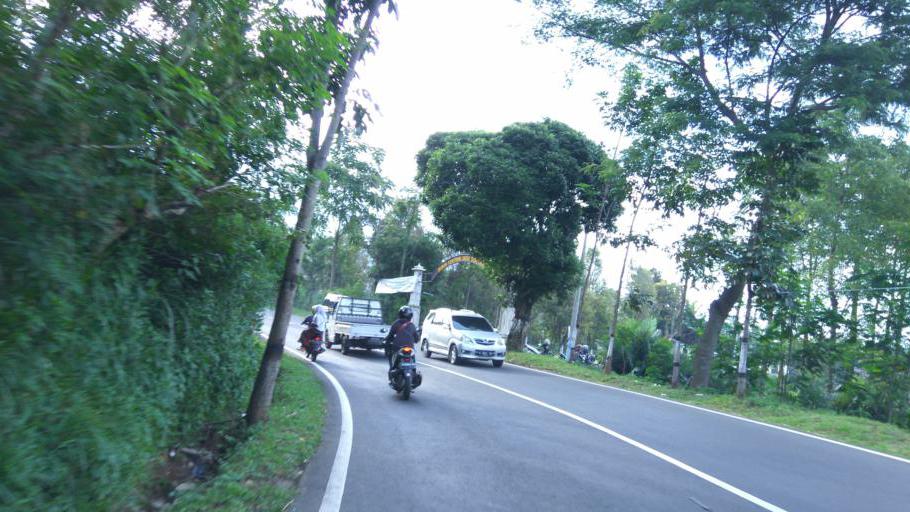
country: ID
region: Central Java
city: Salatiga
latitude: -7.3691
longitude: 110.4533
